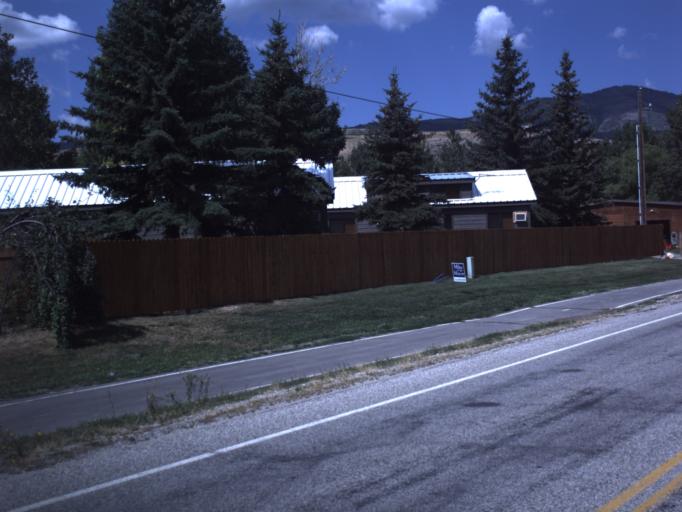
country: US
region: Idaho
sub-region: Bear Lake County
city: Paris
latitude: 41.9550
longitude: -111.3962
